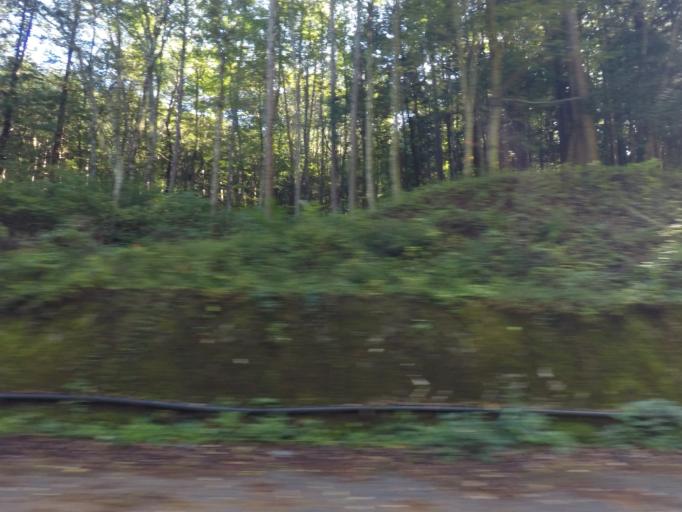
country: JP
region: Nagano
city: Ina
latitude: 35.9562
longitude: 137.7780
